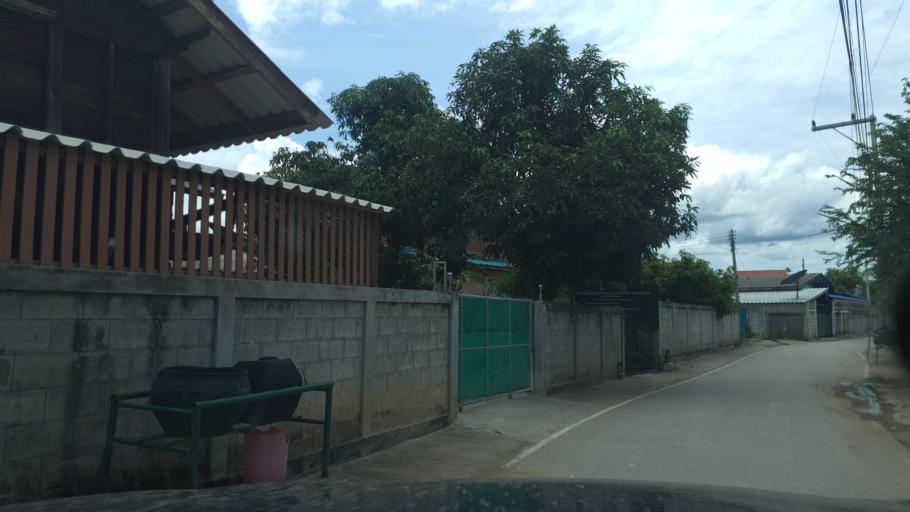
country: TH
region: Lampang
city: Sop Prap
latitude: 17.8789
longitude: 99.3835
